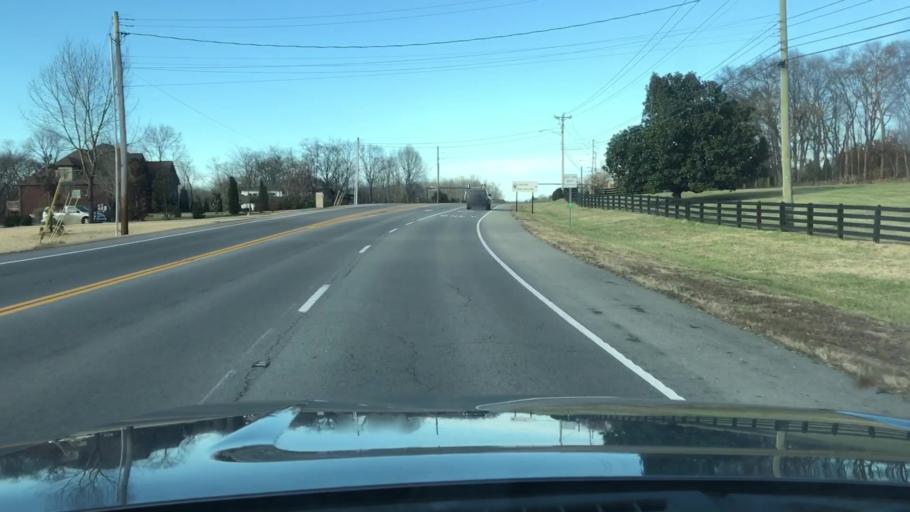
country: US
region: Tennessee
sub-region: Williamson County
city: Brentwood Estates
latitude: 35.9758
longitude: -86.7765
